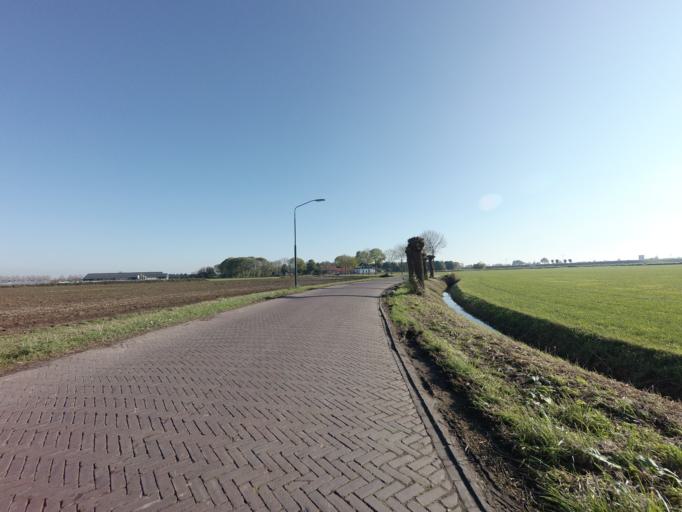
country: NL
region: North Brabant
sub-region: Gemeente Waalwijk
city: Waalwijk
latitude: 51.7180
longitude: 5.0454
